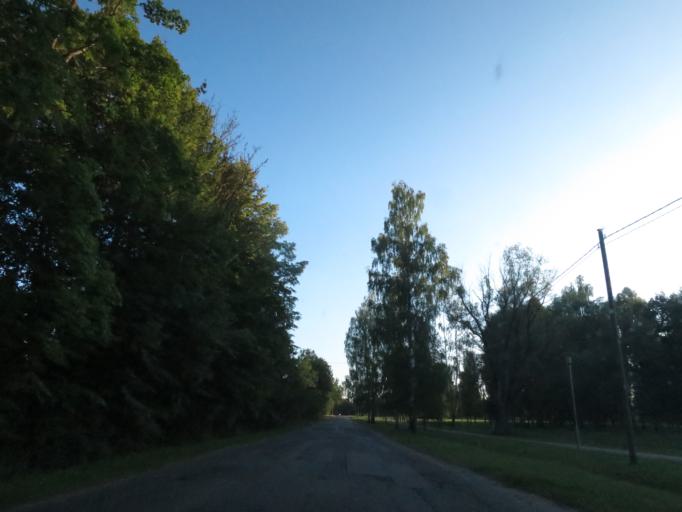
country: LV
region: Sigulda
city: Sigulda
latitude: 57.1645
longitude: 24.8599
